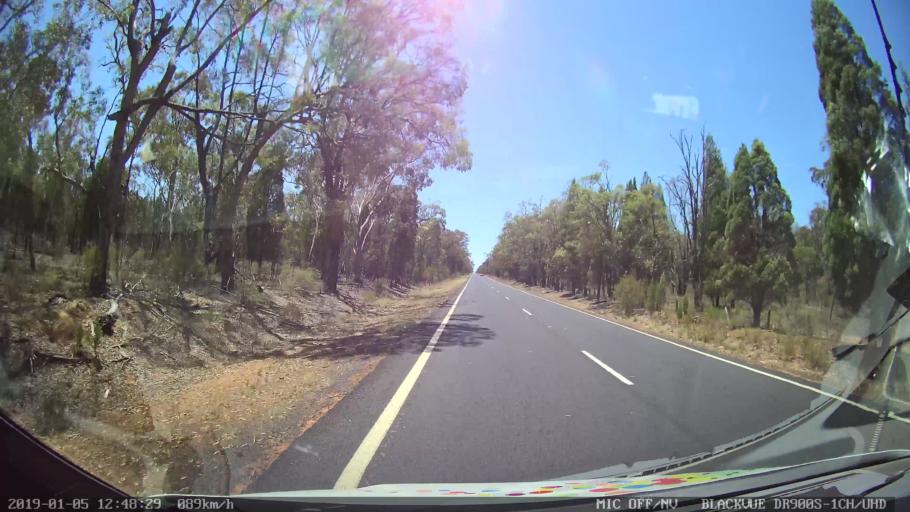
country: AU
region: New South Wales
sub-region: Warrumbungle Shire
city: Coonabarabran
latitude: -31.1180
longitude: 149.5927
